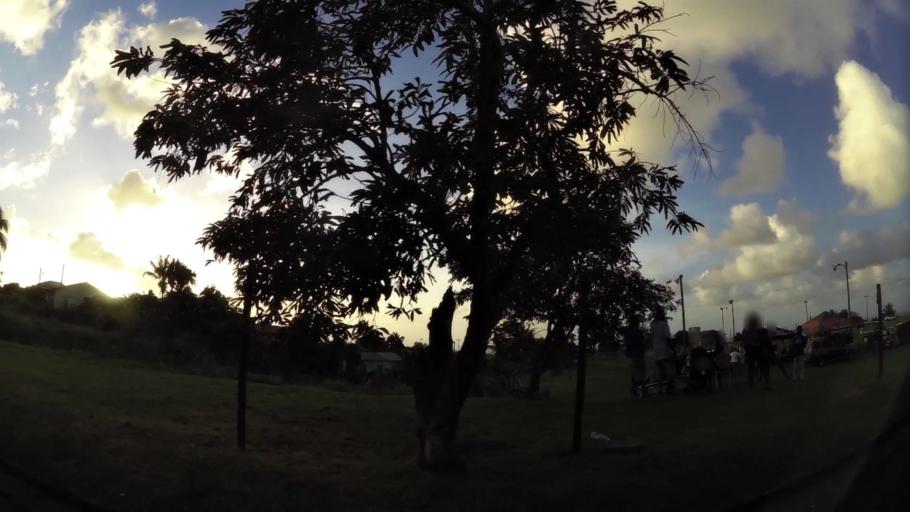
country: KN
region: Saint Paul Capesterre
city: Saint Paul's
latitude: 17.4032
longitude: -62.8368
